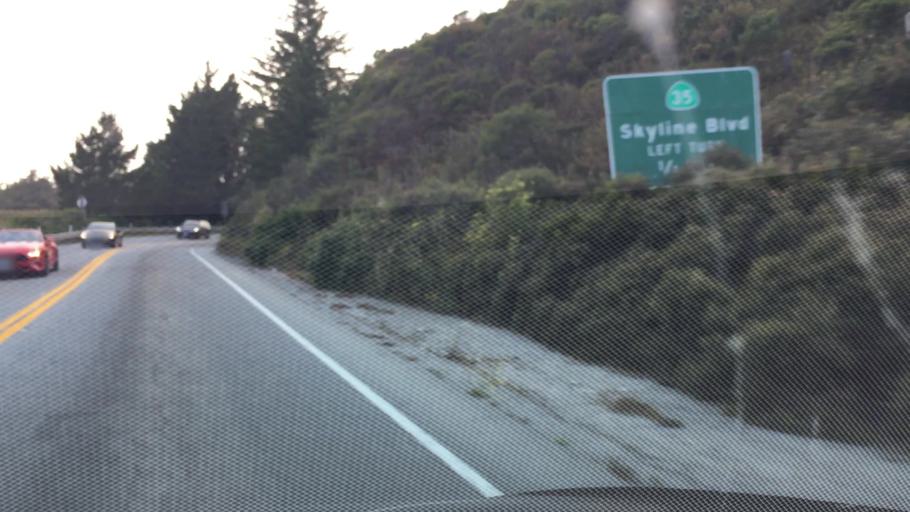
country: US
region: California
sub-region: San Mateo County
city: Highlands-Baywood Park
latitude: 37.4958
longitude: -122.3647
